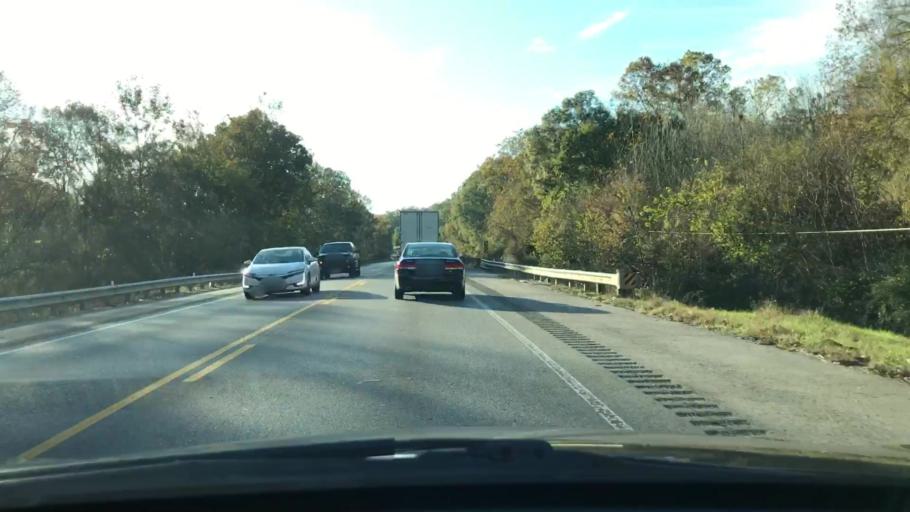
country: US
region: Alabama
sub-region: Calhoun County
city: Choccolocco
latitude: 33.6238
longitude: -85.7235
